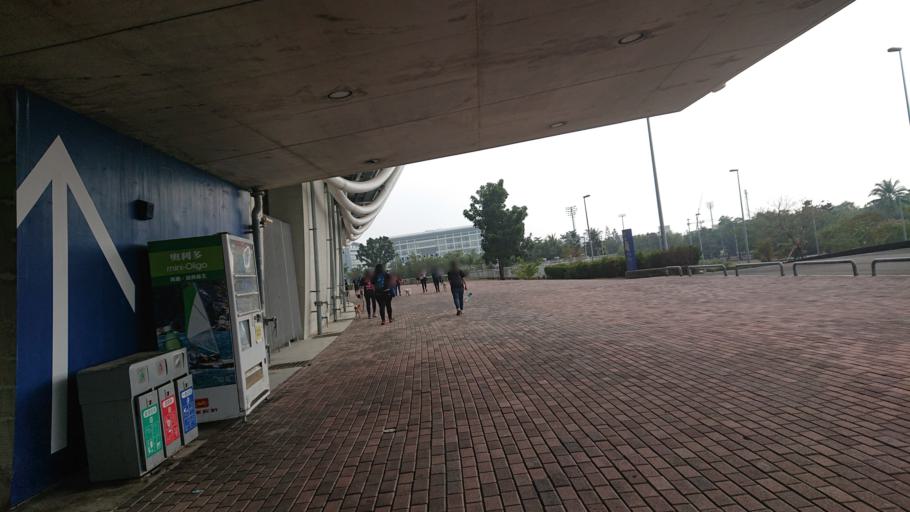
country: TW
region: Kaohsiung
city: Kaohsiung
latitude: 22.7028
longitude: 120.2936
